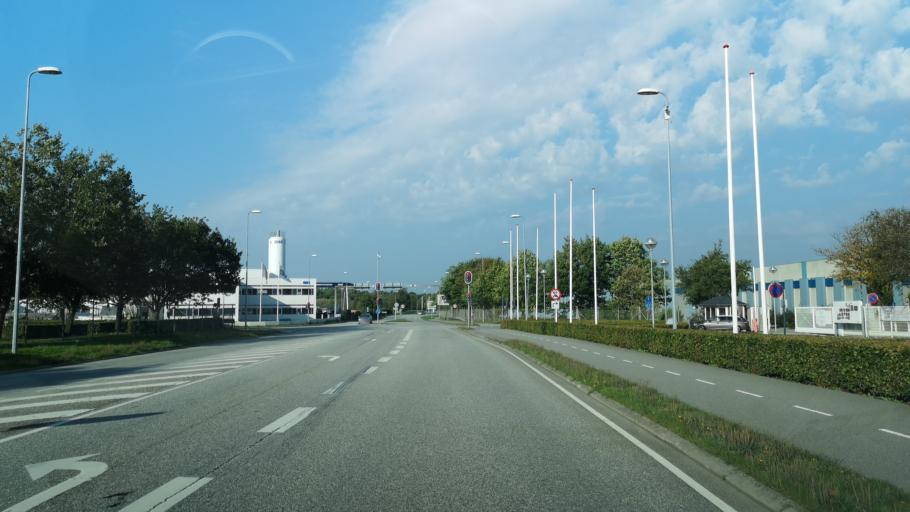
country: DK
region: Central Jutland
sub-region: Herning Kommune
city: Herning
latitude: 56.1225
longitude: 8.9497
